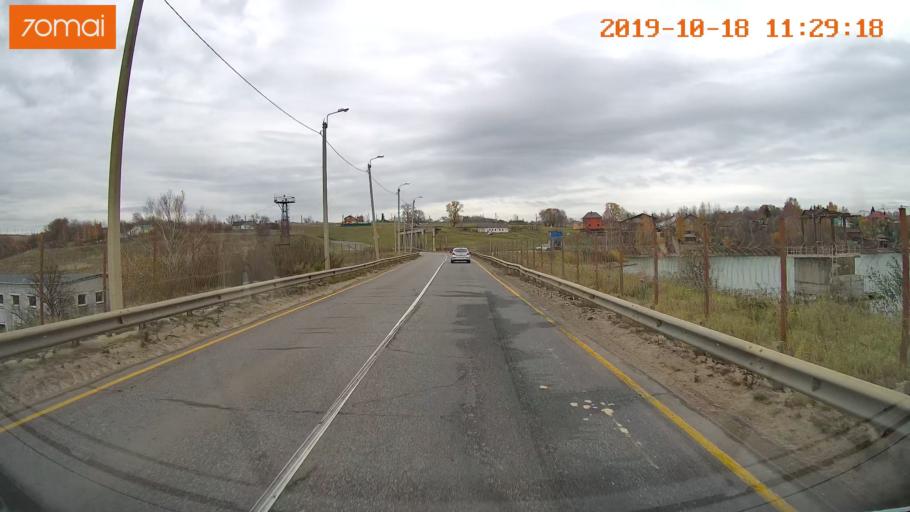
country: RU
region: Rjazan
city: Oktyabr'skiy
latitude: 54.1569
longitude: 38.6753
